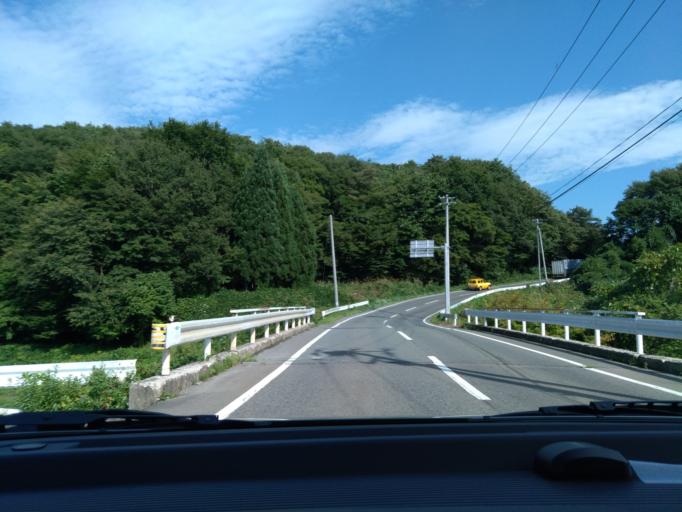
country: JP
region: Iwate
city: Shizukuishi
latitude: 39.6458
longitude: 140.9938
